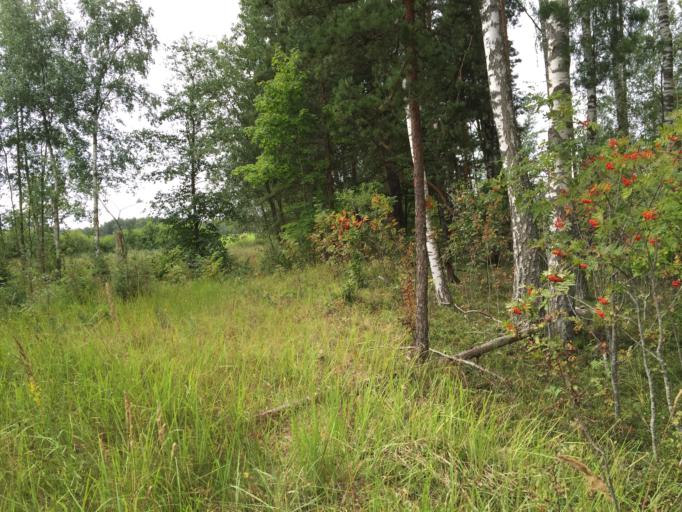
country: LV
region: Jaunpils
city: Jaunpils
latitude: 56.7299
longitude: 23.1569
